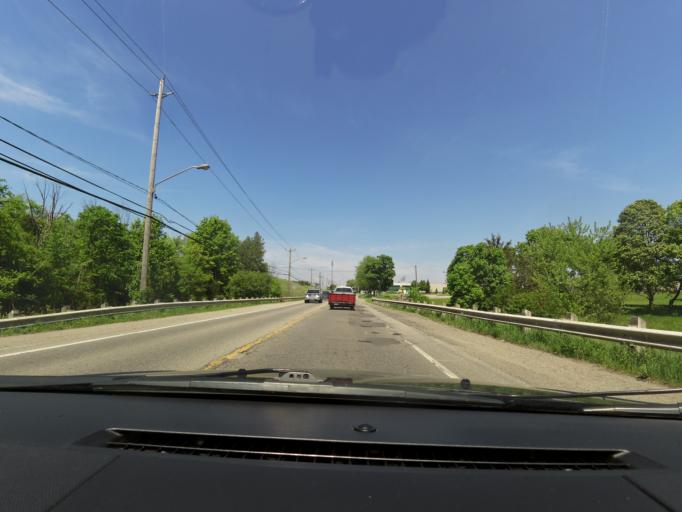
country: CA
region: Ontario
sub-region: Wellington County
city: Guelph
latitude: 43.5608
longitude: -80.2117
